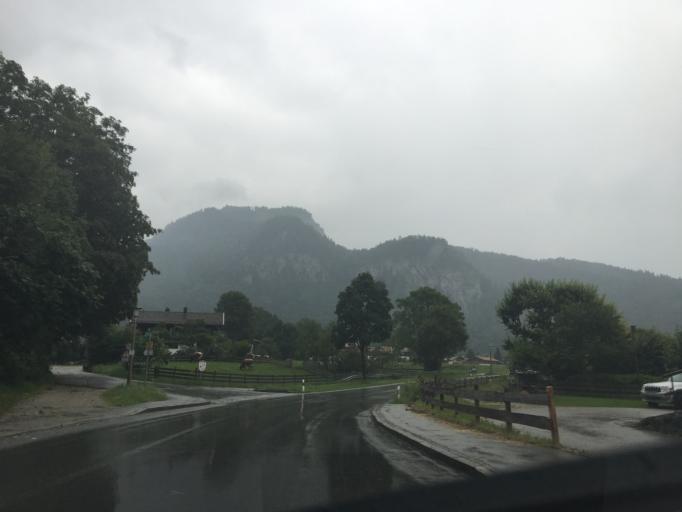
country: DE
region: Bavaria
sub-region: Upper Bavaria
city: Unterwossen
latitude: 47.7141
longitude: 12.4771
